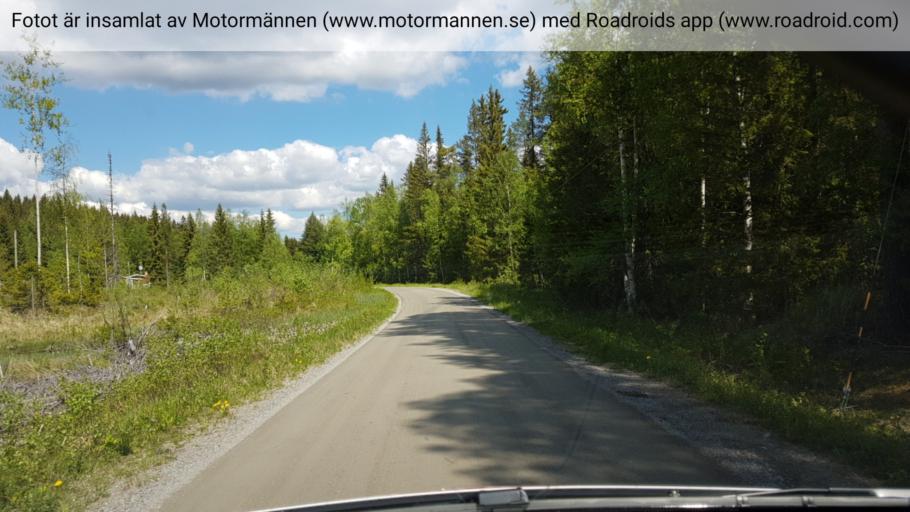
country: SE
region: Jaemtland
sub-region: OEstersunds Kommun
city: Brunflo
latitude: 63.0206
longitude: 15.0747
